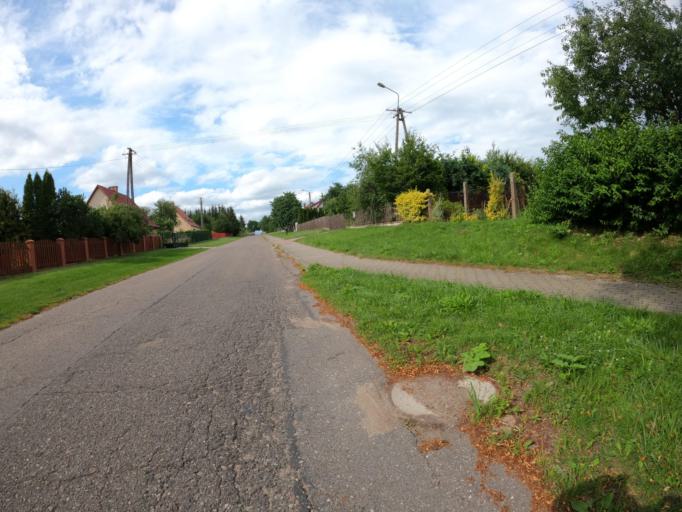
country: PL
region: West Pomeranian Voivodeship
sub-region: Powiat szczecinecki
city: Grzmiaca
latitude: 53.8384
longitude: 16.4350
